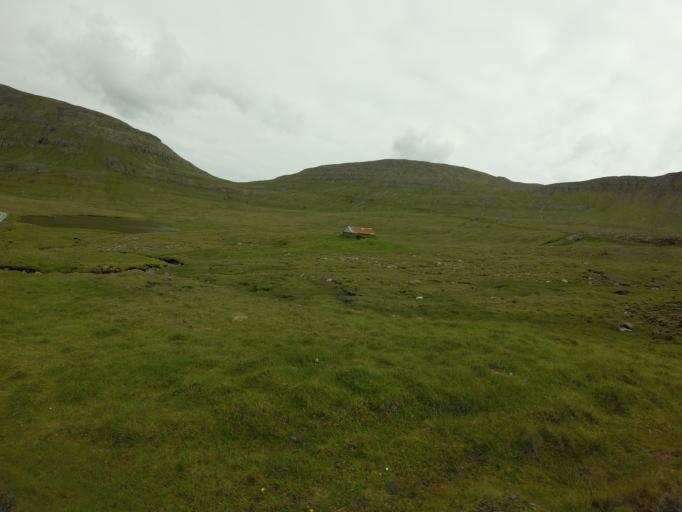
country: FO
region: Suduroy
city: Tvoroyri
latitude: 61.5163
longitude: -6.8478
